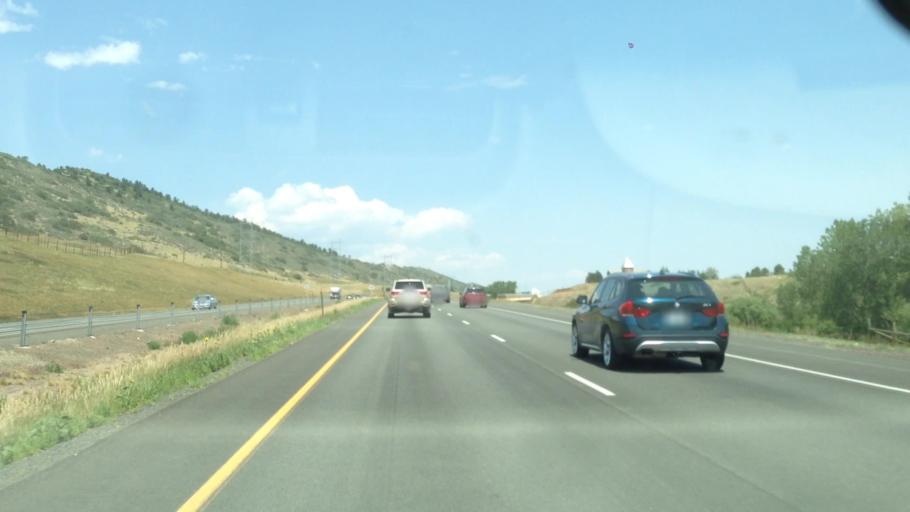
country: US
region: Colorado
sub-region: Jefferson County
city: Ken Caryl
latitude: 39.5980
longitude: -105.1511
